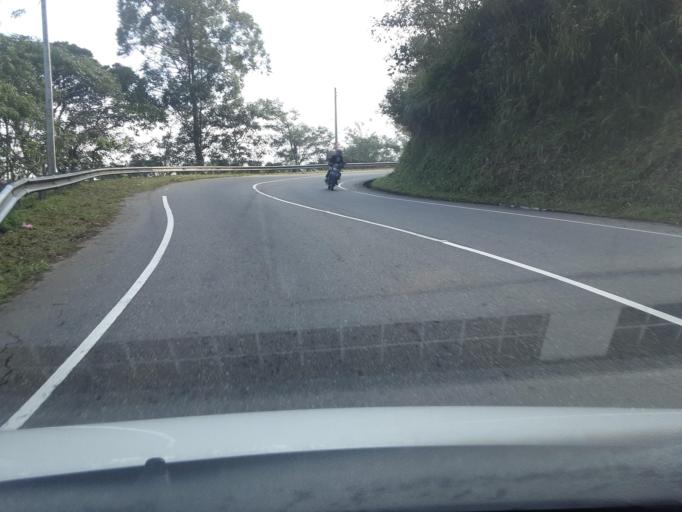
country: LK
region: Uva
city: Badulla
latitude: 6.9198
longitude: 80.9585
